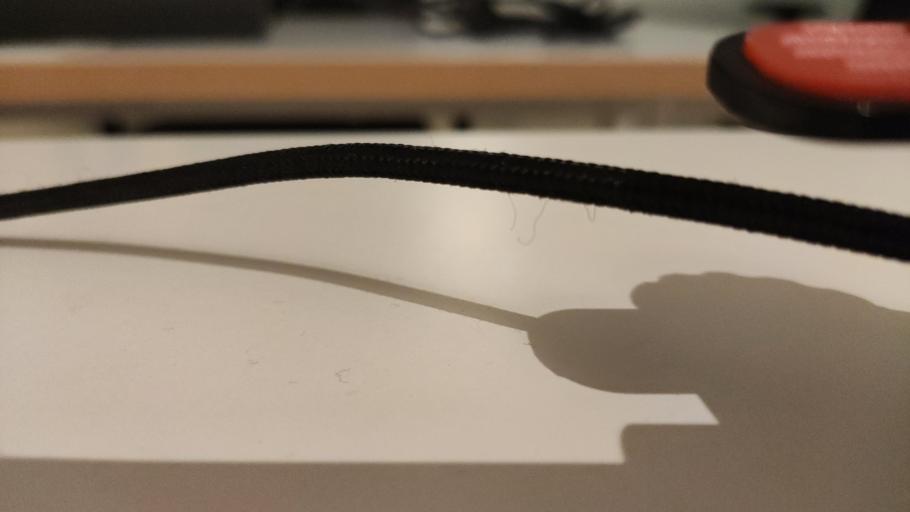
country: RU
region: Moskovskaya
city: Ol'yavidovo
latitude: 56.4264
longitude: 37.7827
